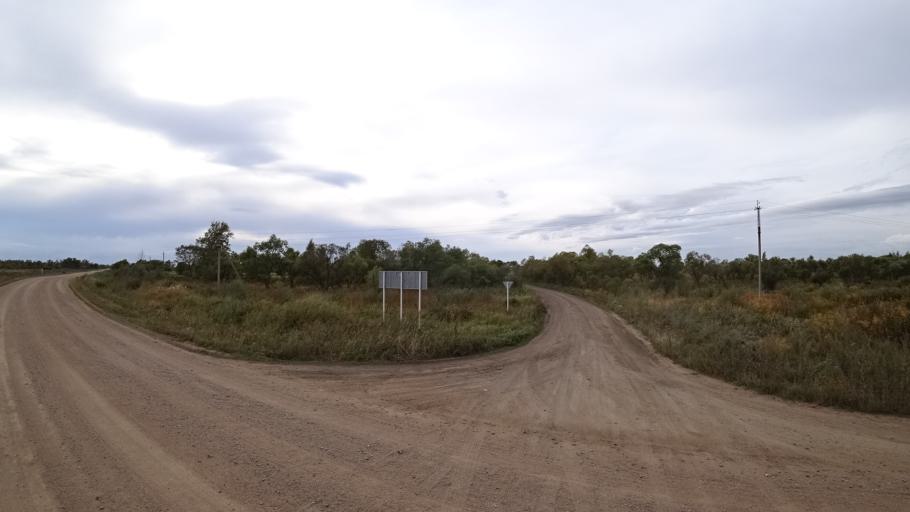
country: RU
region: Amur
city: Arkhara
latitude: 49.3539
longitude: 130.1365
